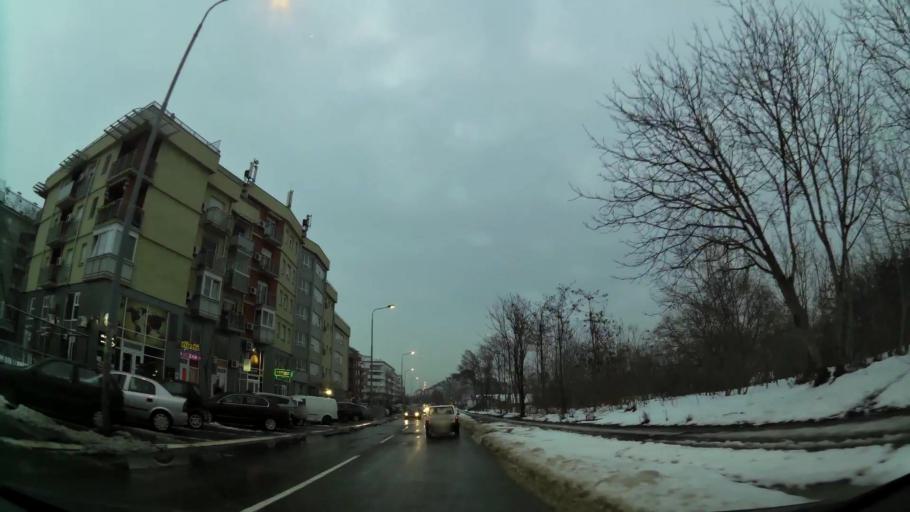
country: RS
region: Central Serbia
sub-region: Belgrade
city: Zemun
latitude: 44.8114
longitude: 20.3694
